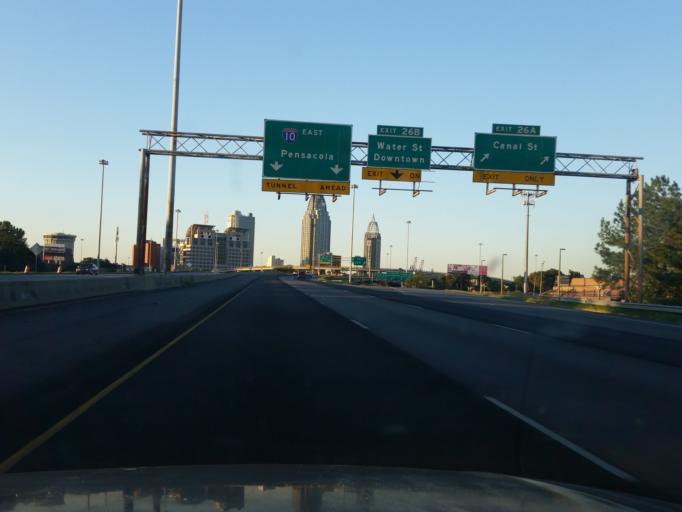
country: US
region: Alabama
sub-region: Mobile County
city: Mobile
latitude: 30.6805
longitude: -88.0430
